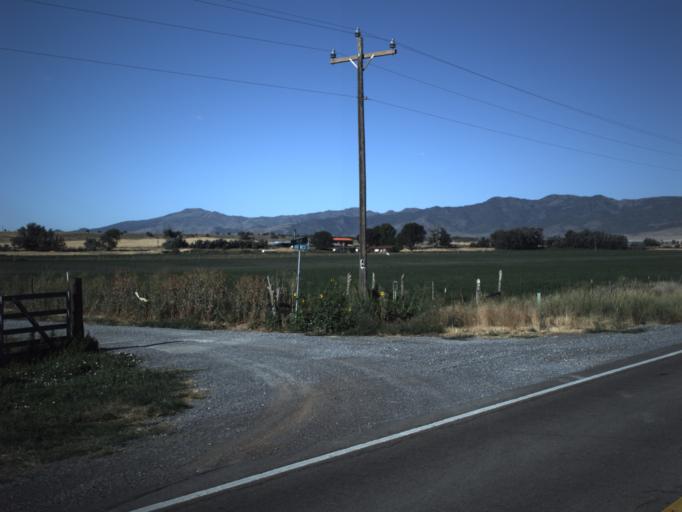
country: US
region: Utah
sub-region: Utah County
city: Genola
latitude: 39.9525
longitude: -111.9090
